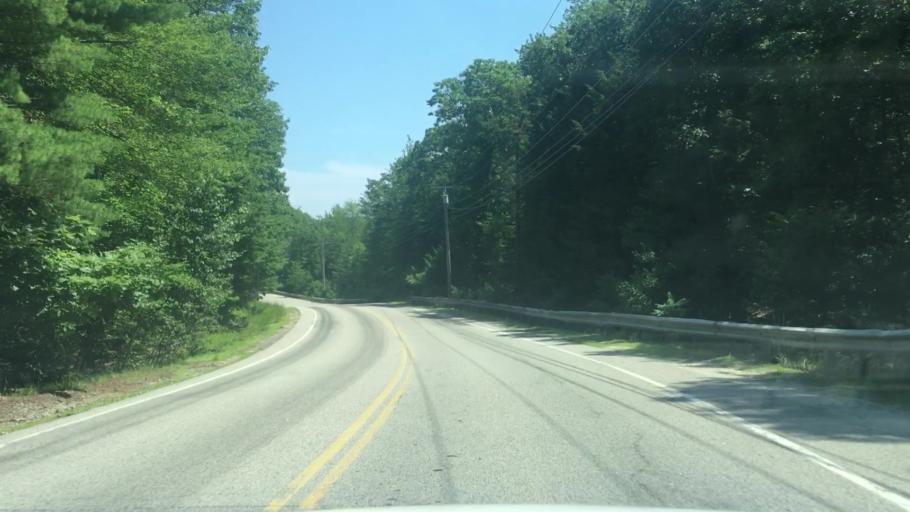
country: US
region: Maine
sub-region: Cumberland County
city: Falmouth
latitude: 43.7361
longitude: -70.2451
